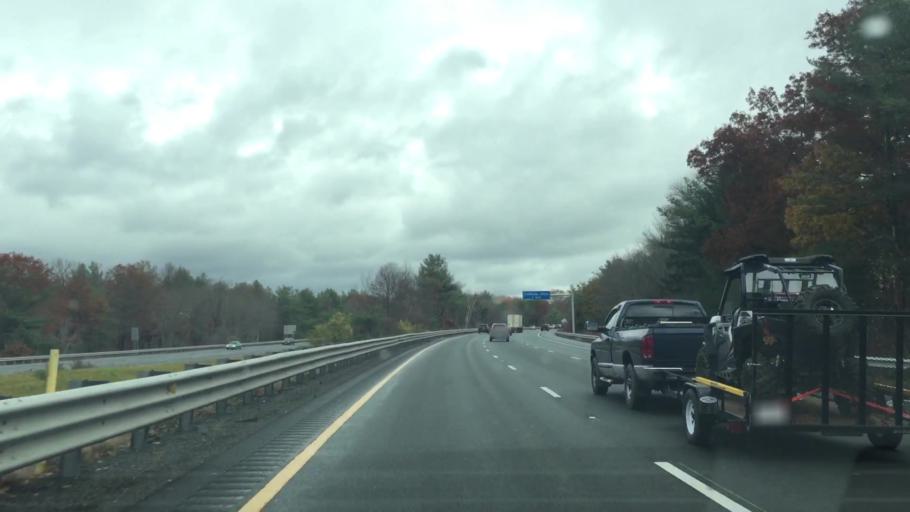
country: US
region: Massachusetts
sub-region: Essex County
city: Haverhill
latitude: 42.8045
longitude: -71.0837
